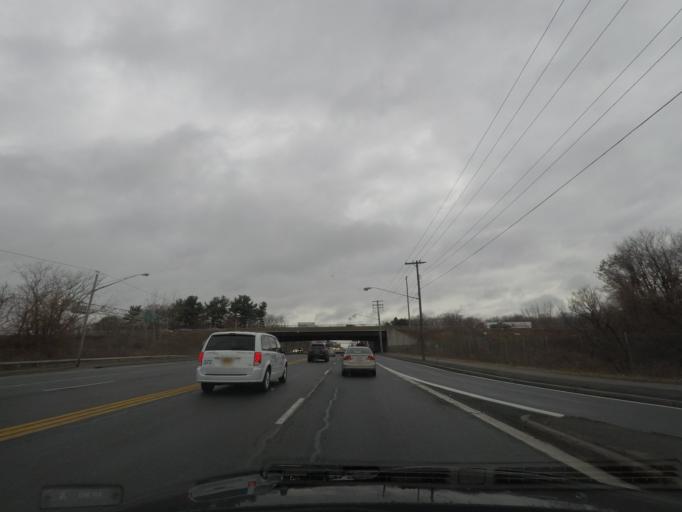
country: US
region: New York
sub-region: Albany County
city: Colonie
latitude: 42.7099
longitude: -73.8239
